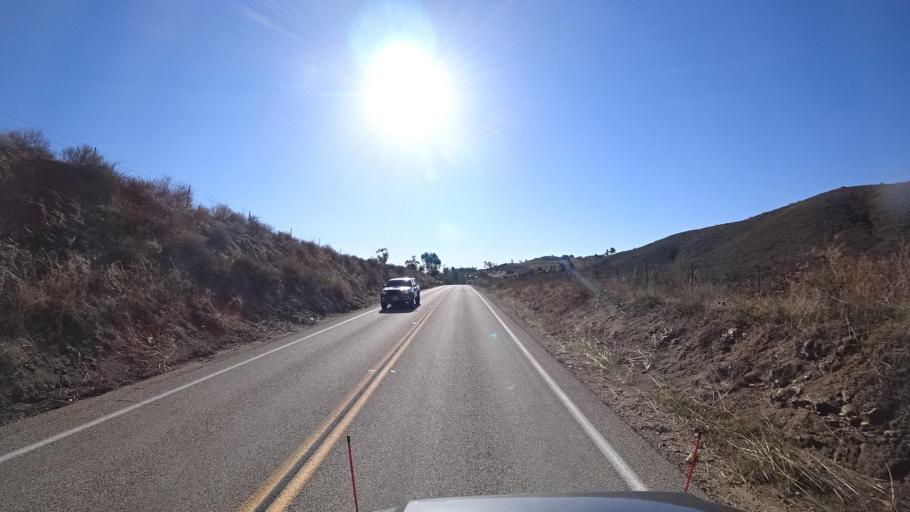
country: US
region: California
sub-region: San Diego County
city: Jamul
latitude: 32.6673
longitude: -116.7988
